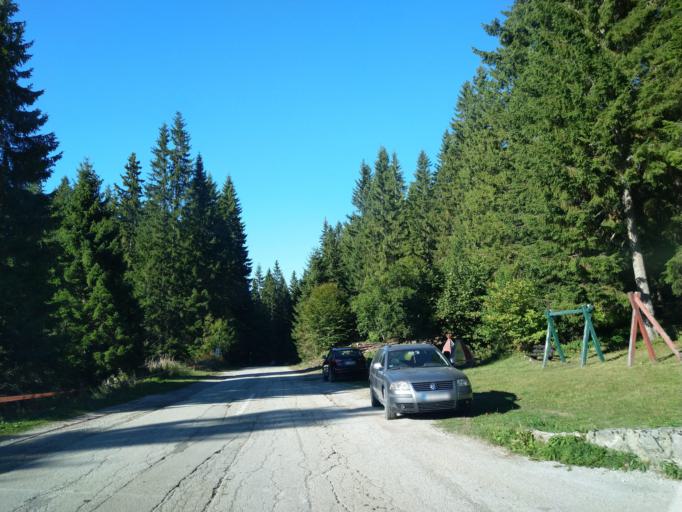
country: RS
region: Central Serbia
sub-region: Moravicki Okrug
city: Ivanjica
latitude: 43.4239
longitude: 20.2637
